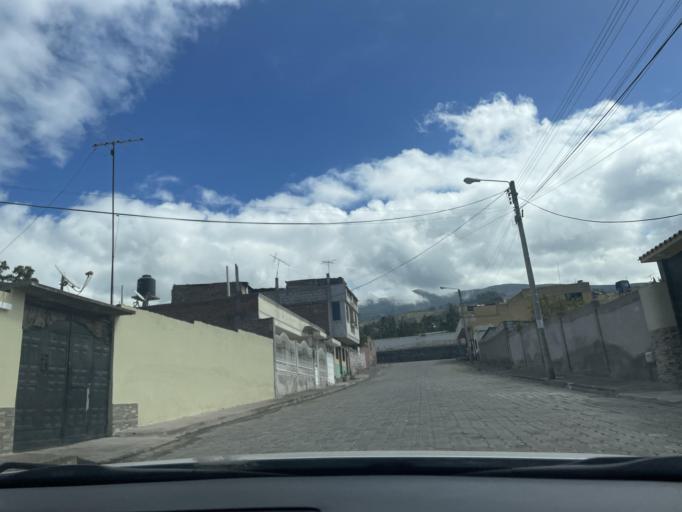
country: EC
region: Chimborazo
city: Guano
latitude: -1.6033
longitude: -78.6438
